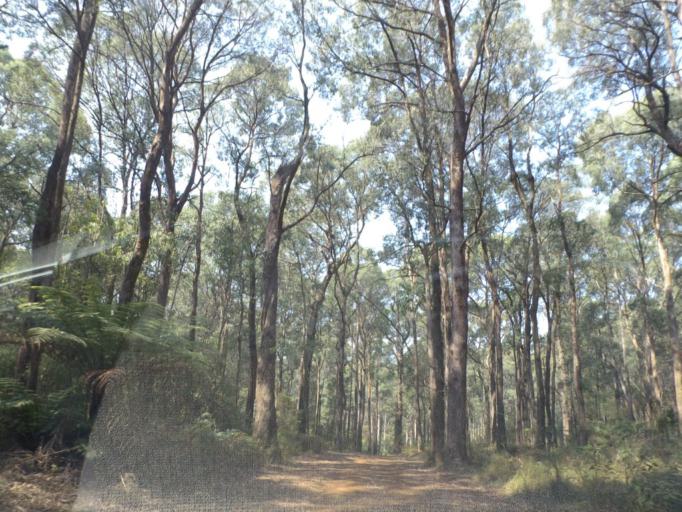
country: AU
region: Victoria
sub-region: Yarra Ranges
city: Healesville
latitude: -37.5853
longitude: 145.6704
